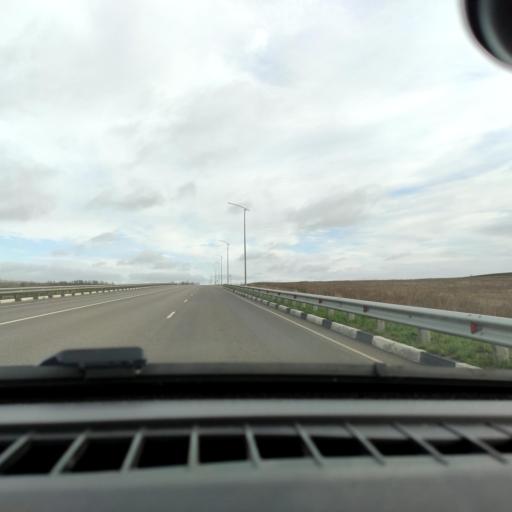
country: RU
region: Belgorod
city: Ilovka
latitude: 50.6668
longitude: 38.5983
